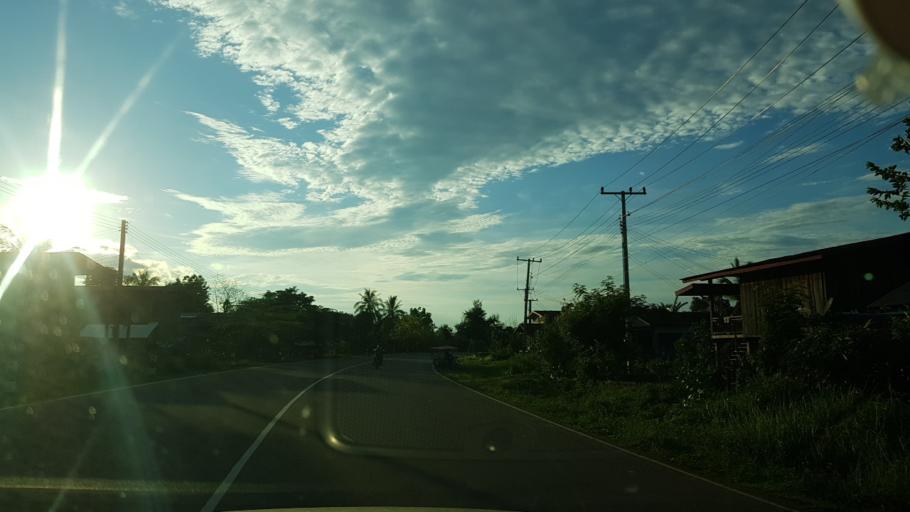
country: TH
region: Nong Khai
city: Sangkhom
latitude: 18.0586
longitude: 102.3004
